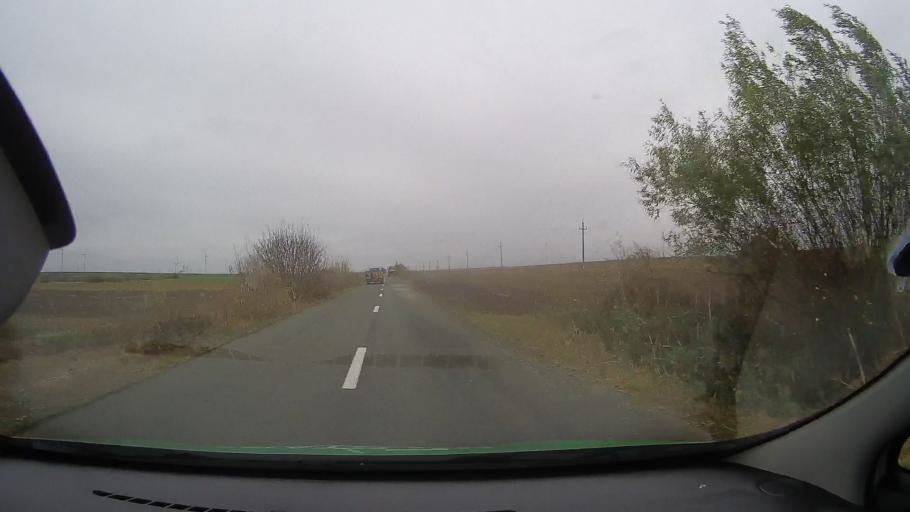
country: RO
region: Constanta
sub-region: Comuna Targusor
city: Targusor
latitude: 44.4695
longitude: 28.3895
